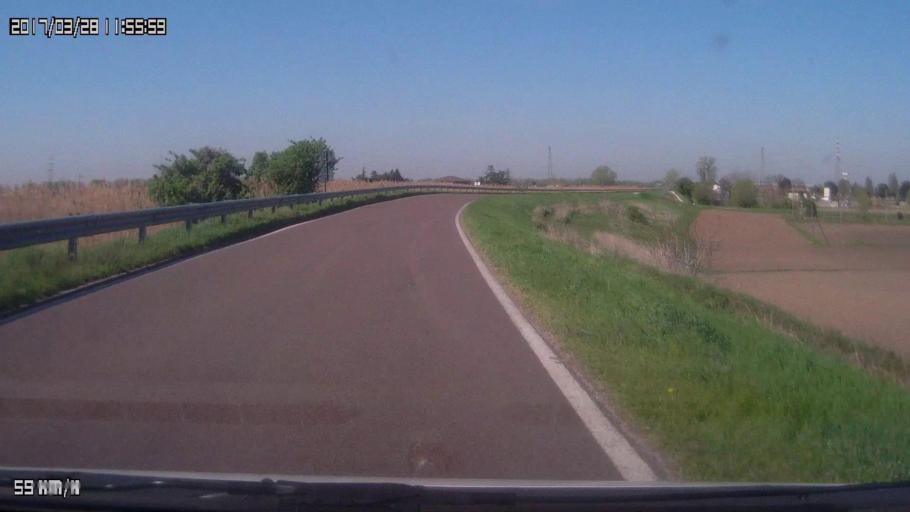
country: IT
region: Veneto
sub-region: Provincia di Venezia
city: Boscochiaro
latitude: 45.1323
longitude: 12.1438
